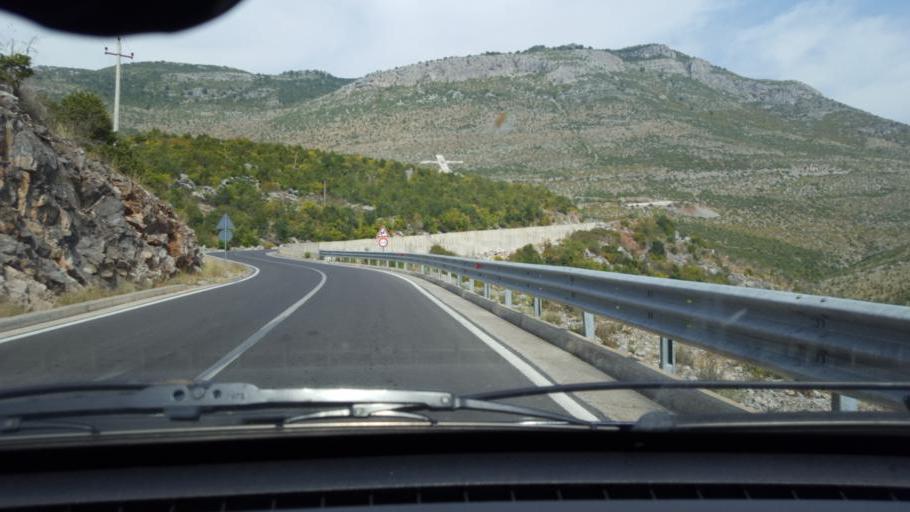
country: AL
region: Shkoder
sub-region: Rrethi i Malesia e Madhe
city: Hot
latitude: 42.3681
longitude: 19.4480
